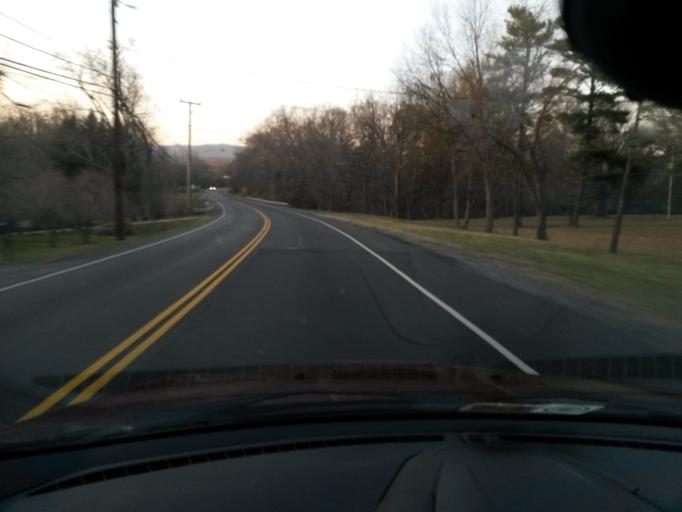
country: US
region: Virginia
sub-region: Roanoke County
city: Hollins
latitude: 37.3439
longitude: -79.9467
